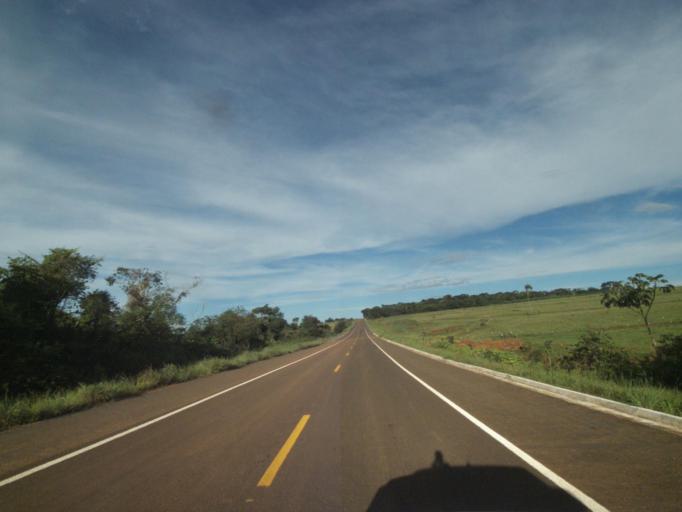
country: BR
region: Goias
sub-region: Jaragua
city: Jaragua
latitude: -15.8932
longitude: -49.4917
